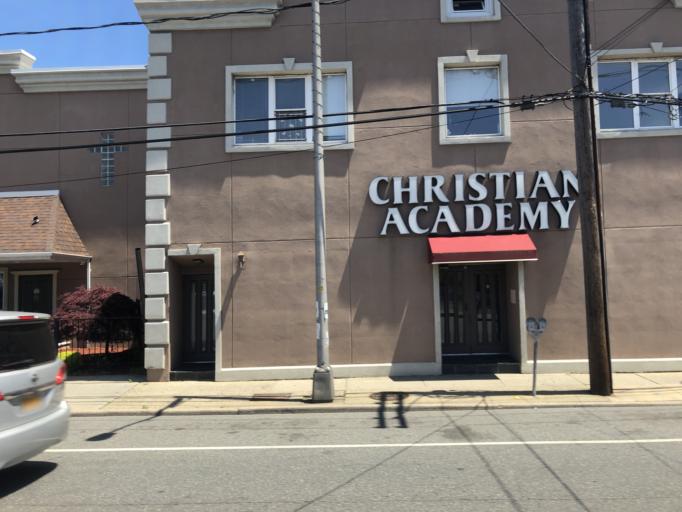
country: US
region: New York
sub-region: Nassau County
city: Freeport
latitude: 40.6587
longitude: -73.5845
